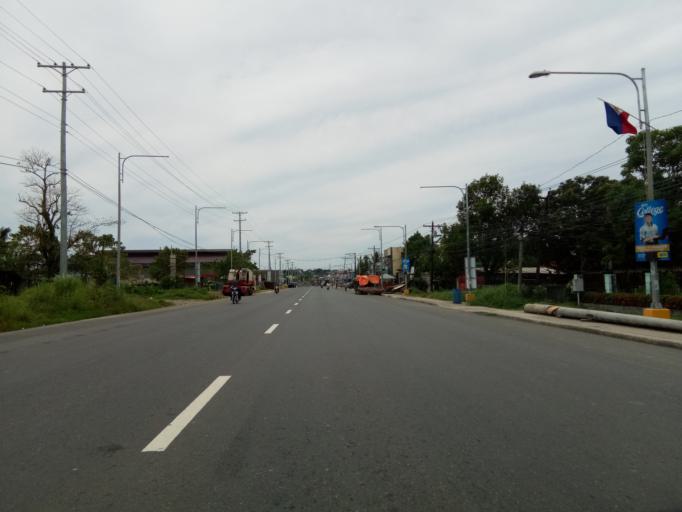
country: PH
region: Caraga
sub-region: Province of Surigao del Norte
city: Rizal
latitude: 9.7668
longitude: 125.4832
